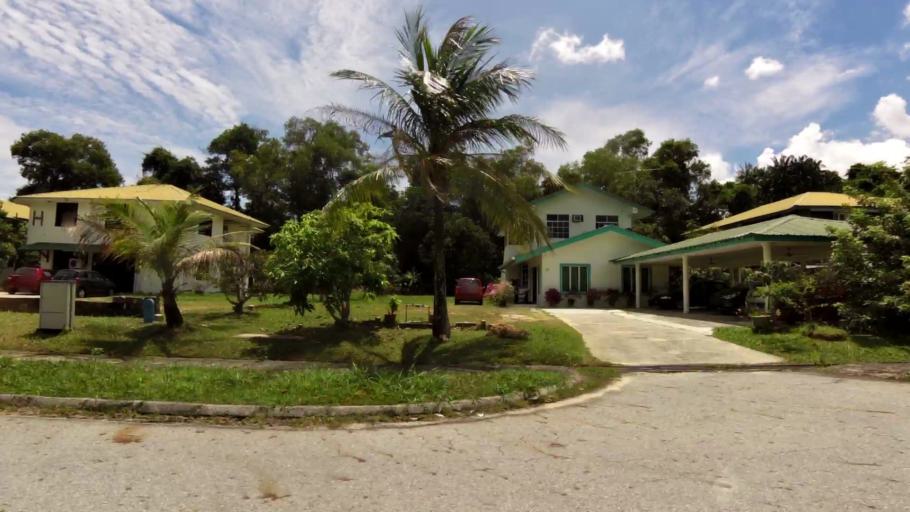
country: BN
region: Brunei and Muara
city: Bandar Seri Begawan
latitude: 4.9613
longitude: 114.9052
